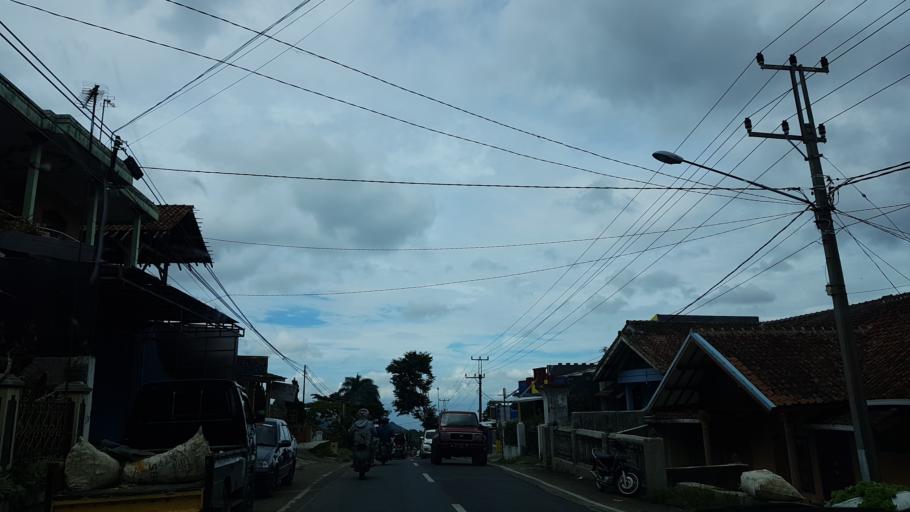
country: ID
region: West Java
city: Banjar
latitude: -7.1163
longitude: 107.4362
